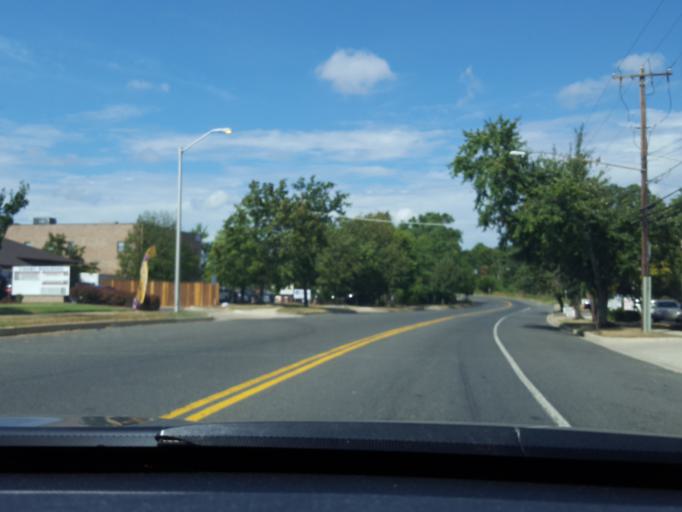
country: US
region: Maryland
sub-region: Prince George's County
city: Andrews AFB
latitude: 38.7808
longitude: -76.8766
